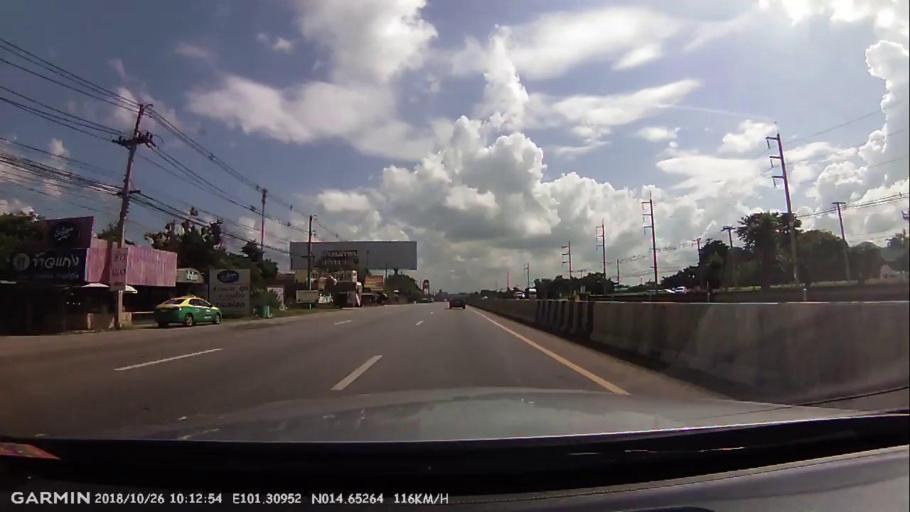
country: TH
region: Sara Buri
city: Muak Lek
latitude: 14.6529
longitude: 101.3097
